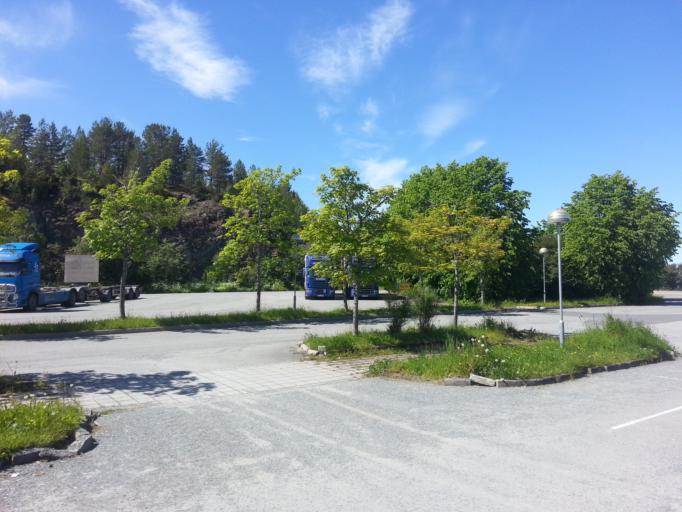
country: NO
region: Sor-Trondelag
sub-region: Malvik
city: Malvik
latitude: 63.4234
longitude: 10.7279
